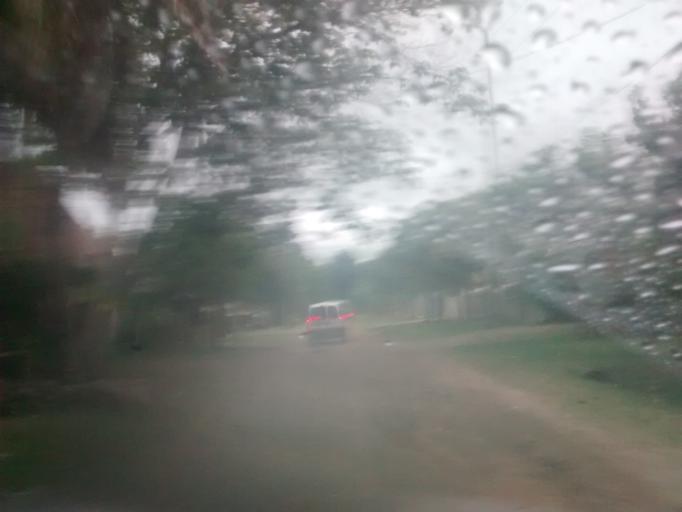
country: AR
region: Buenos Aires
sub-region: Partido de La Plata
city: La Plata
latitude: -34.8844
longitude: -58.0641
